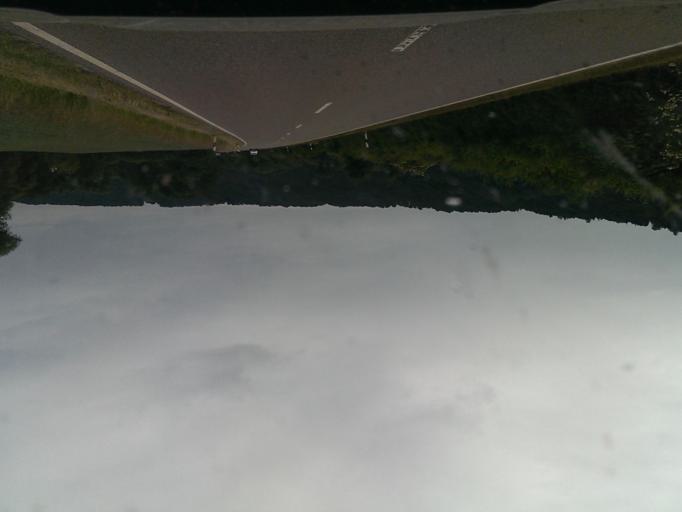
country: DE
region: Bavaria
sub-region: Upper Bavaria
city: Denkendorf
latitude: 49.0114
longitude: 11.4488
